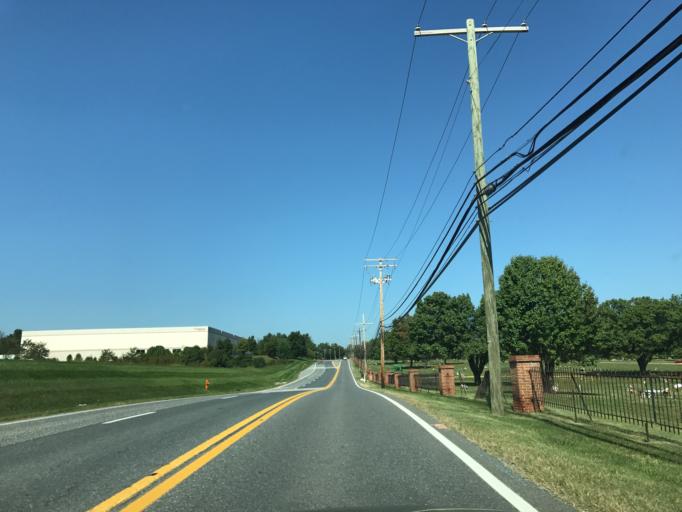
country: US
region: Maryland
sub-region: Anne Arundel County
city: Jessup
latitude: 39.1856
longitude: -76.7653
